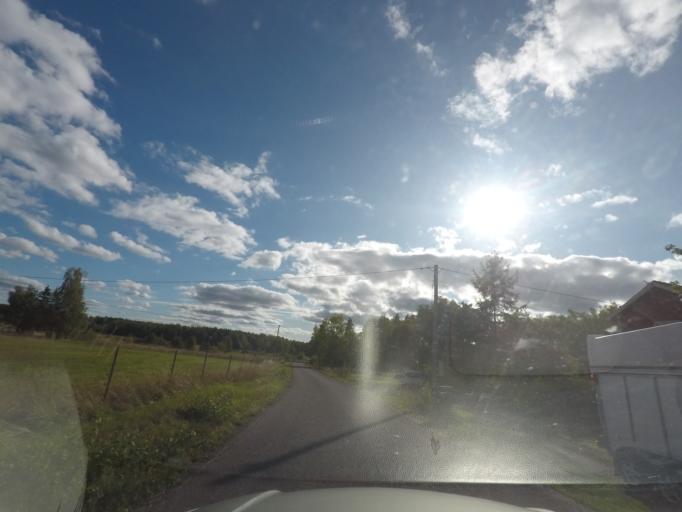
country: SE
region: Vaestmanland
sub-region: Hallstahammars Kommun
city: Kolback
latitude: 59.5032
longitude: 16.1914
